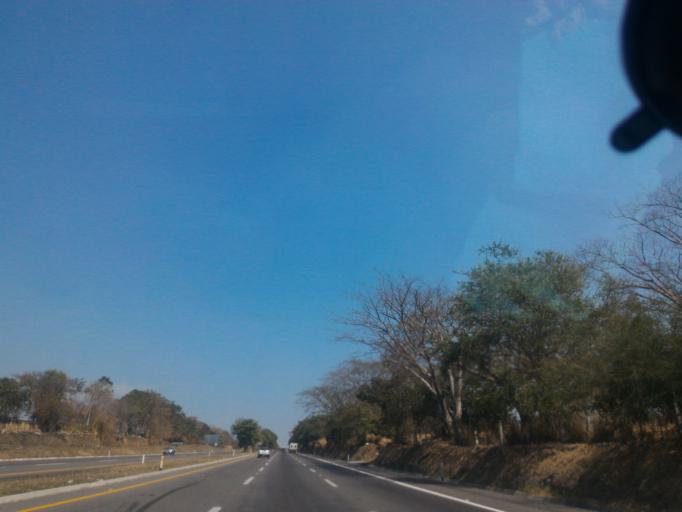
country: MX
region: Colima
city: Cuauhtemoc
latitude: 19.2963
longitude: -103.6434
